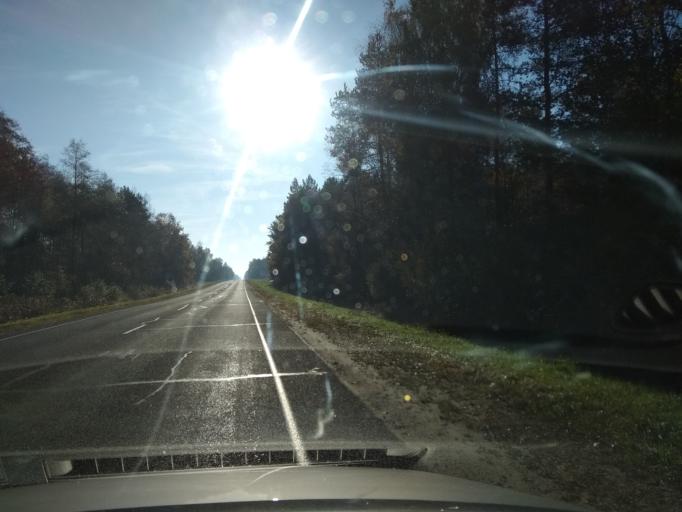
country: BY
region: Brest
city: Malaryta
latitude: 51.8888
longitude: 24.1463
